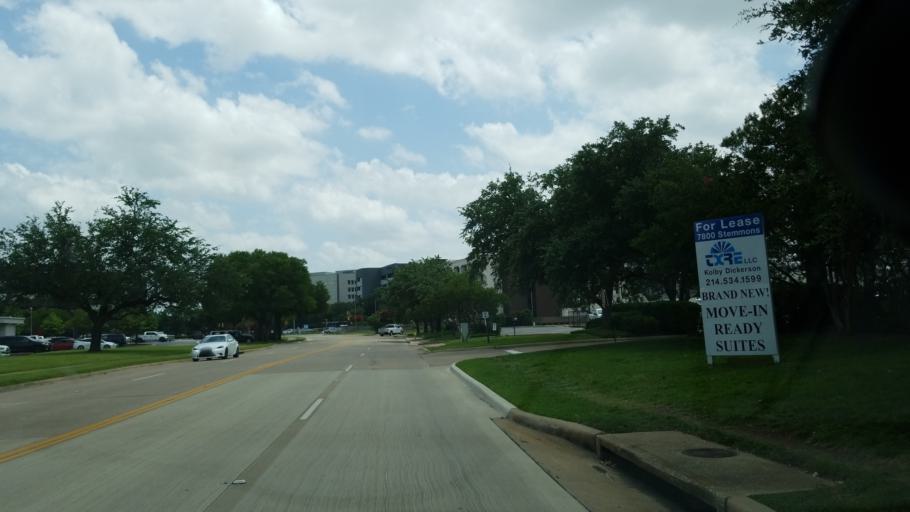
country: US
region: Texas
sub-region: Dallas County
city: Dallas
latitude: 32.8223
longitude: -96.8678
